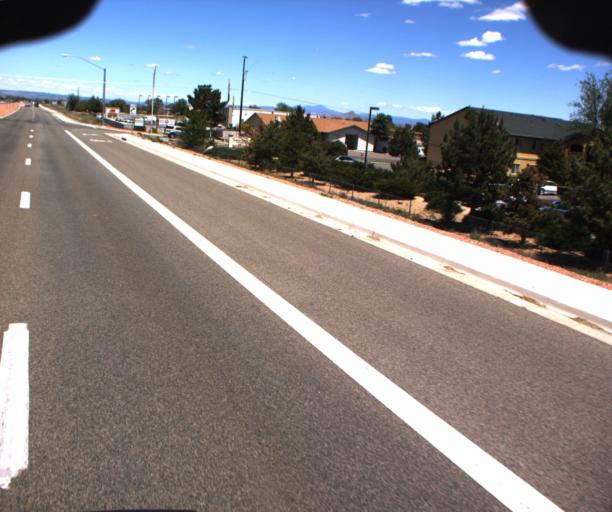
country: US
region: Arizona
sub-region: Yavapai County
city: Chino Valley
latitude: 34.7230
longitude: -112.4536
